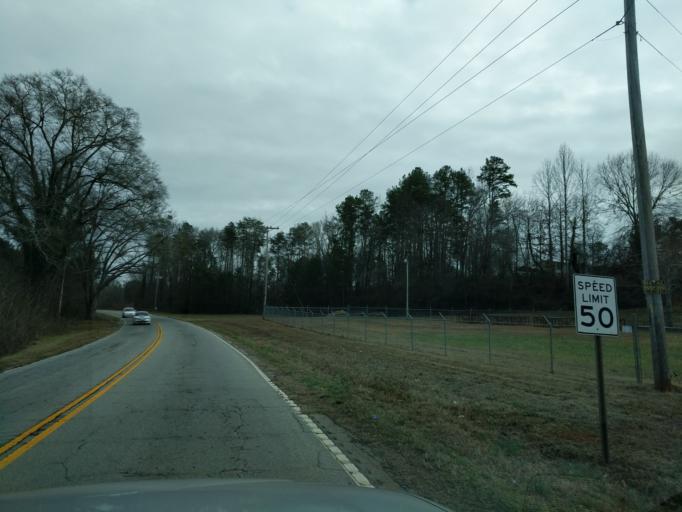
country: US
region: South Carolina
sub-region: Oconee County
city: Westminster
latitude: 34.6507
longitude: -83.0818
